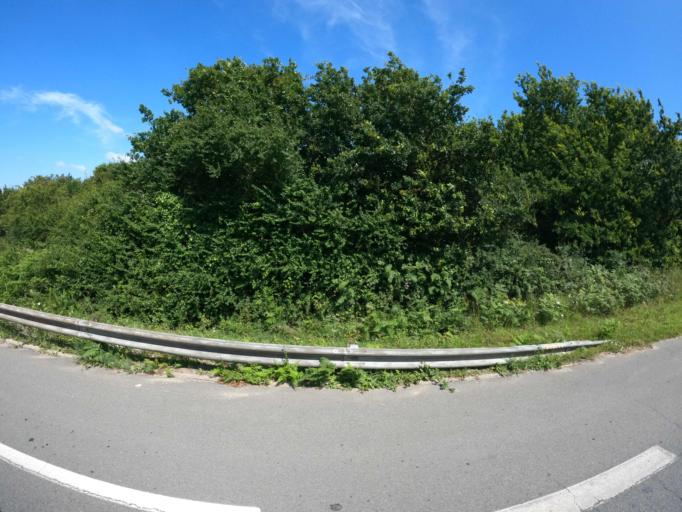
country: FR
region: Pays de la Loire
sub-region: Departement de la Loire-Atlantique
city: Saint-Nazaire
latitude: 47.2815
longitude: -2.2490
